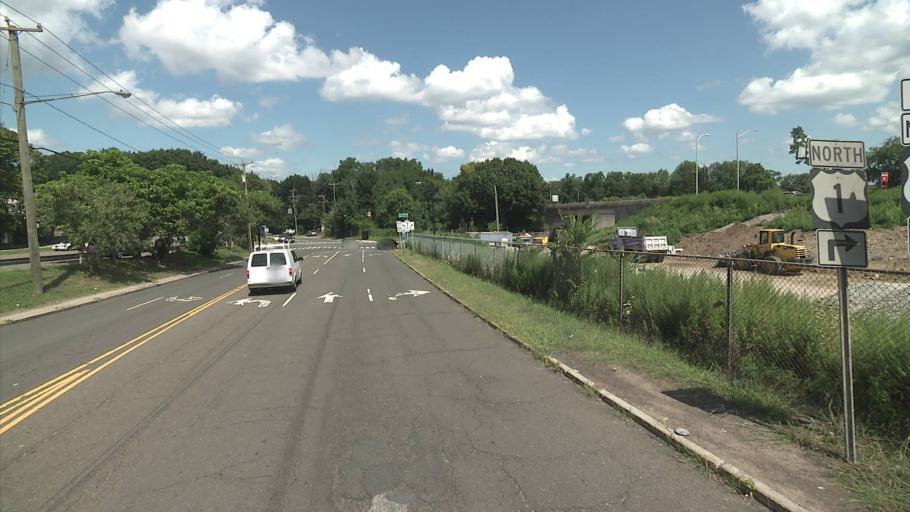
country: US
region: Connecticut
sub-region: Fairfield County
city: Norwalk
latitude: 41.1173
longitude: -73.4207
